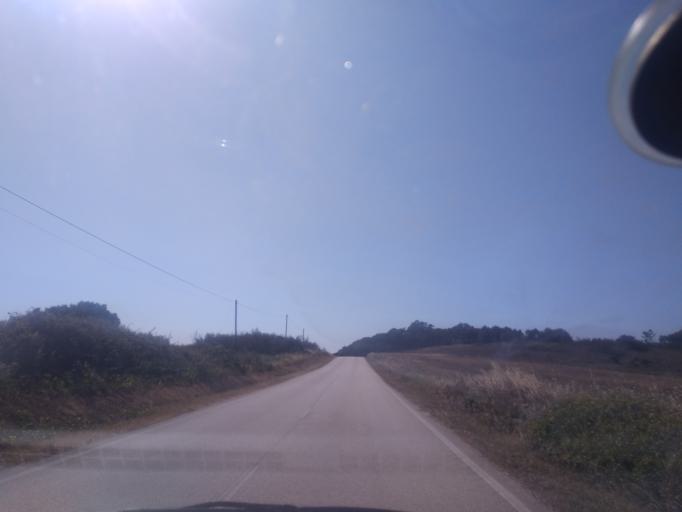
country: PT
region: Faro
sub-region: Aljezur
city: Aljezur
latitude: 37.2249
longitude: -8.8107
